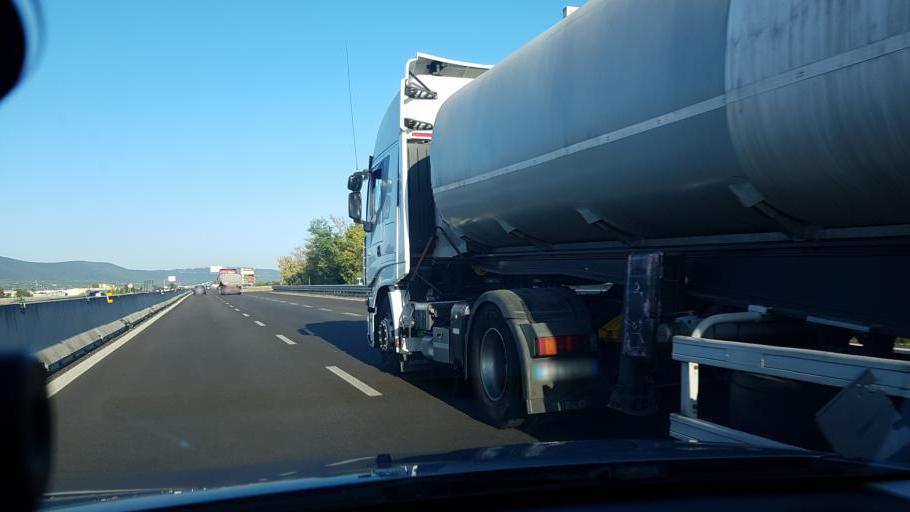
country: IT
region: Apulia
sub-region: Provincia di Brindisi
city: Fasano
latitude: 40.8392
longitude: 17.3764
